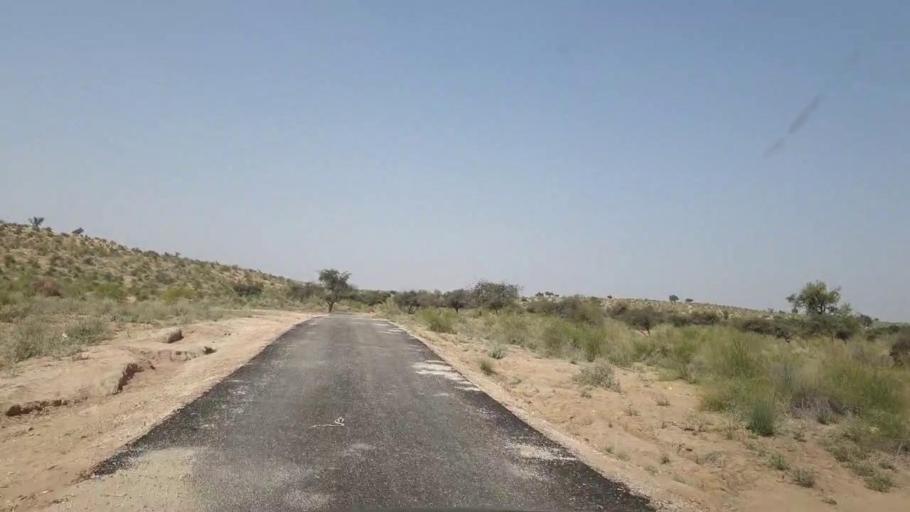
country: PK
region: Sindh
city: Islamkot
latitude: 25.1212
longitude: 70.6515
